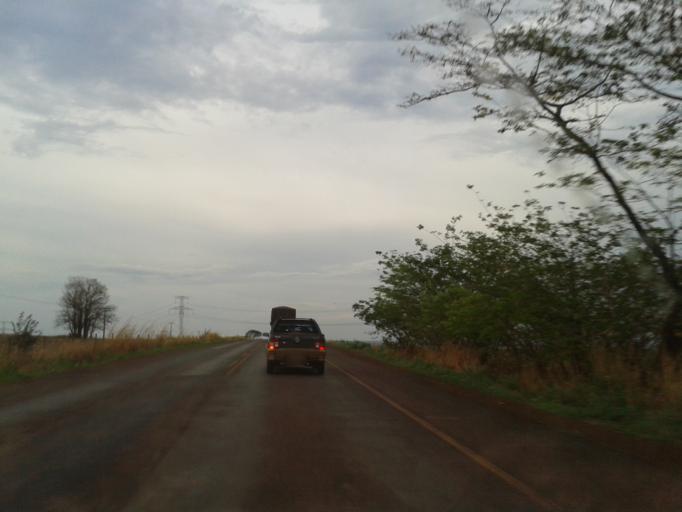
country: BR
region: Goias
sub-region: Santa Helena De Goias
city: Santa Helena de Goias
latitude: -18.0072
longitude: -50.5029
